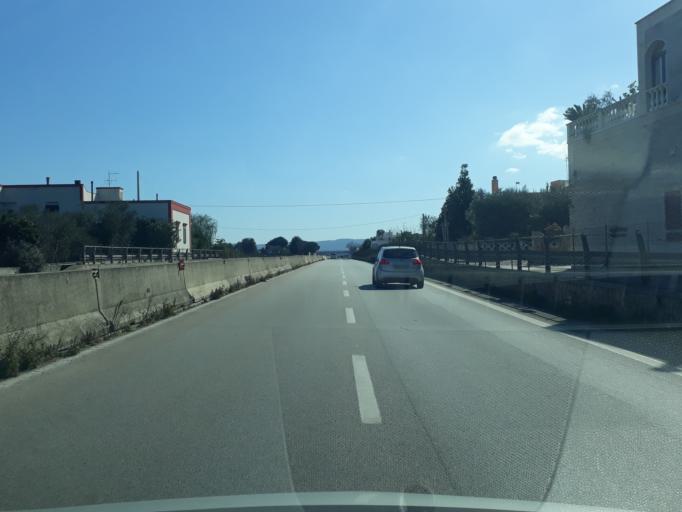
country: IT
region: Apulia
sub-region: Provincia di Brindisi
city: Fasano
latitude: 40.8798
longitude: 17.3385
